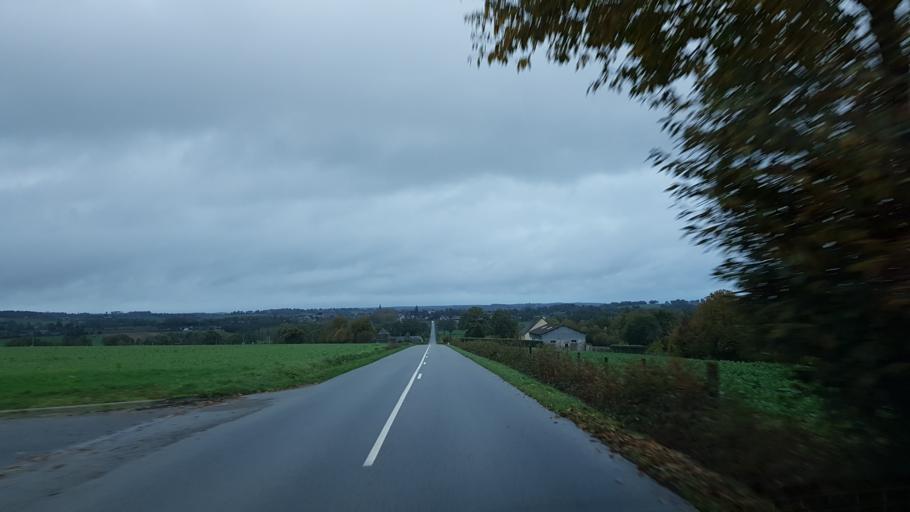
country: FR
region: Brittany
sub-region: Departement d'Ille-et-Vilaine
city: Balaze
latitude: 48.1618
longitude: -1.1351
